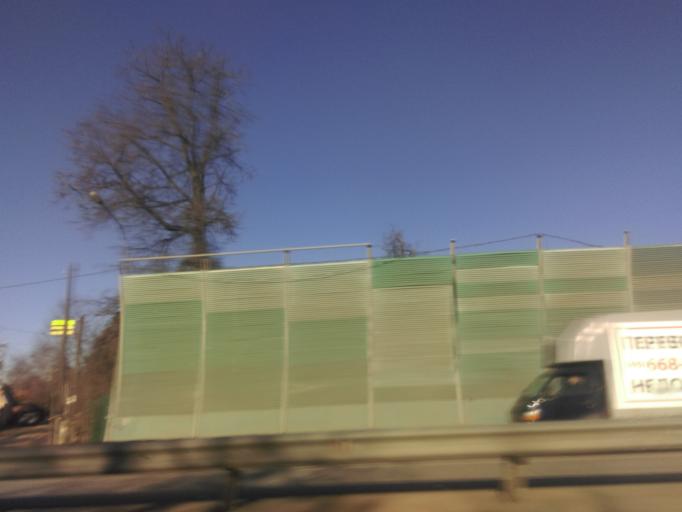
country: RU
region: Moscow
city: Novo-Peredelkino
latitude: 55.6731
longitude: 37.3151
